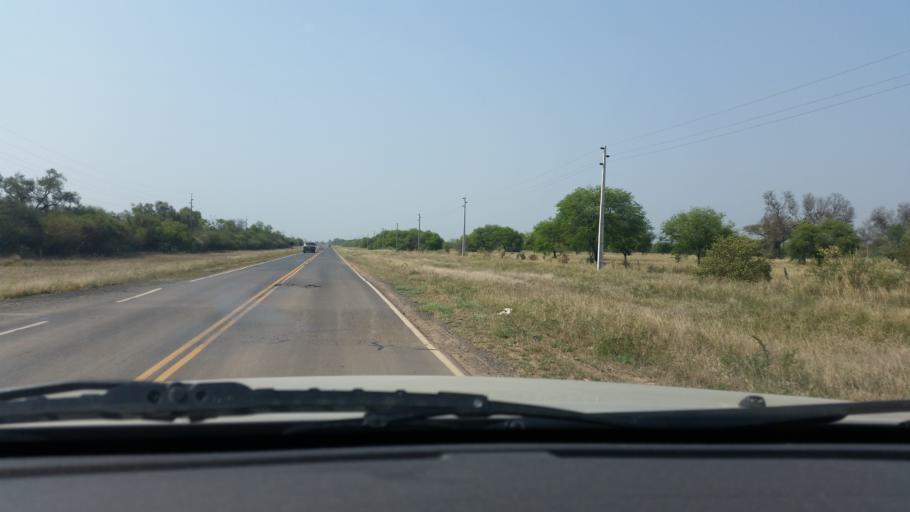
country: PY
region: Boqueron
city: Filadelfia
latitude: -22.4132
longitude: -60.0339
